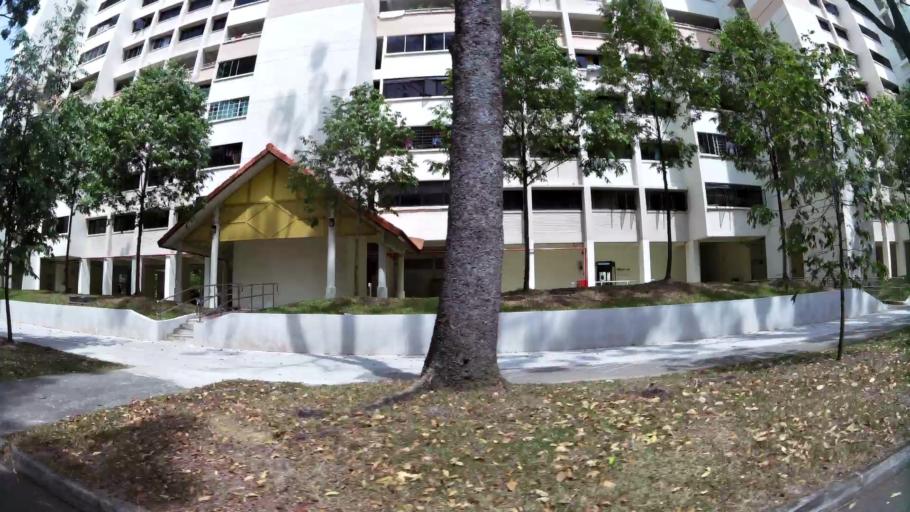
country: MY
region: Johor
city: Johor Bahru
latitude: 1.3493
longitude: 103.7208
